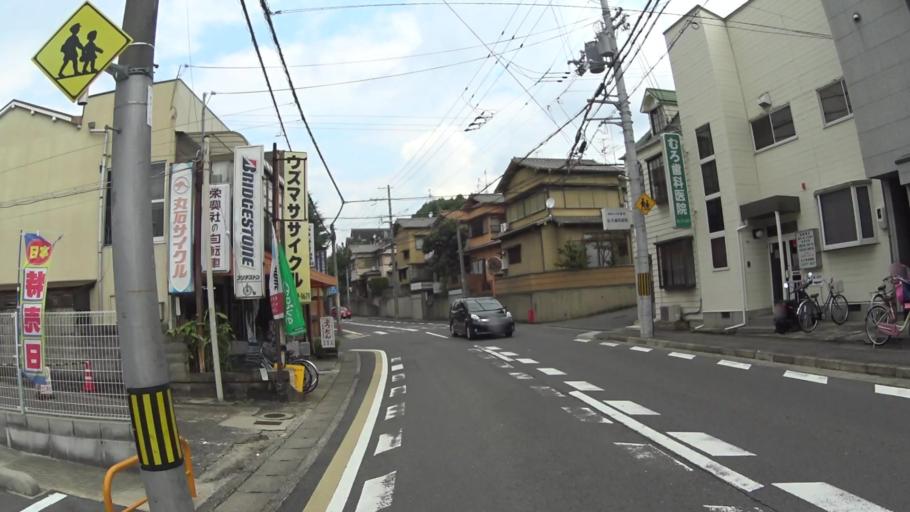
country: JP
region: Kyoto
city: Muko
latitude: 35.0108
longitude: 135.7084
